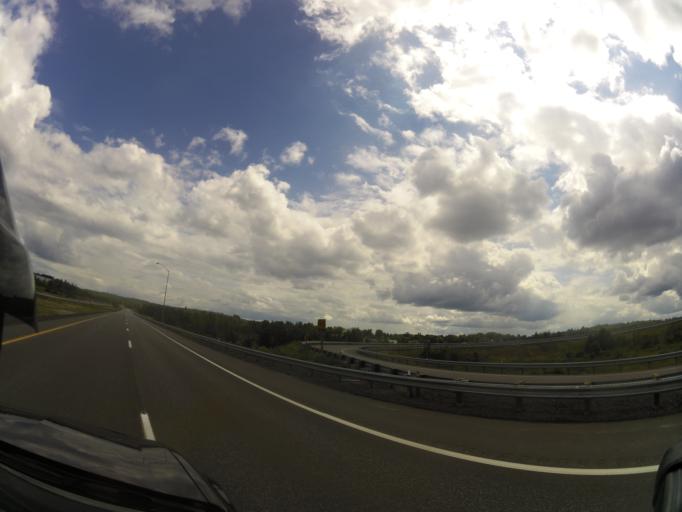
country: CA
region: Ontario
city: Greater Sudbury
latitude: 46.4274
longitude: -81.1206
